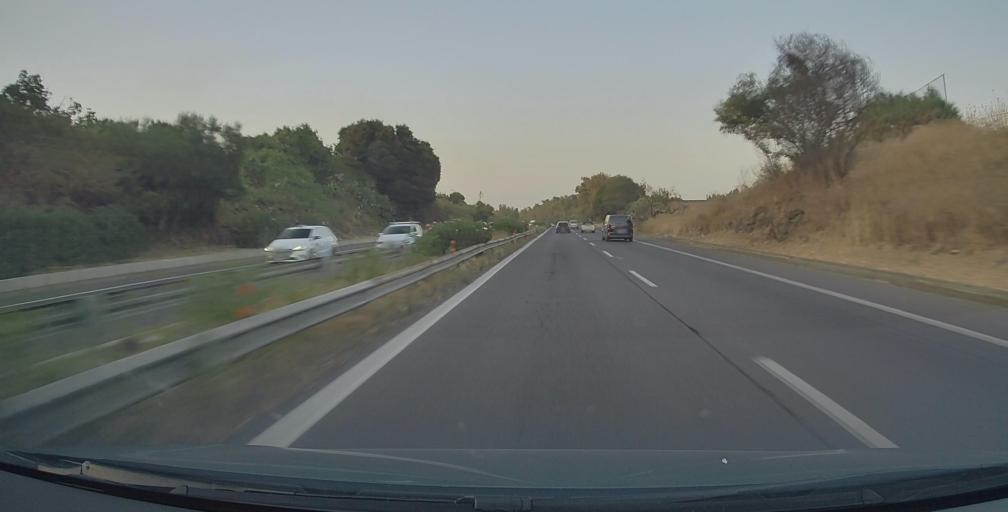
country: IT
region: Sicily
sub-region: Catania
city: Maugeri
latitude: 37.5794
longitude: 15.1173
